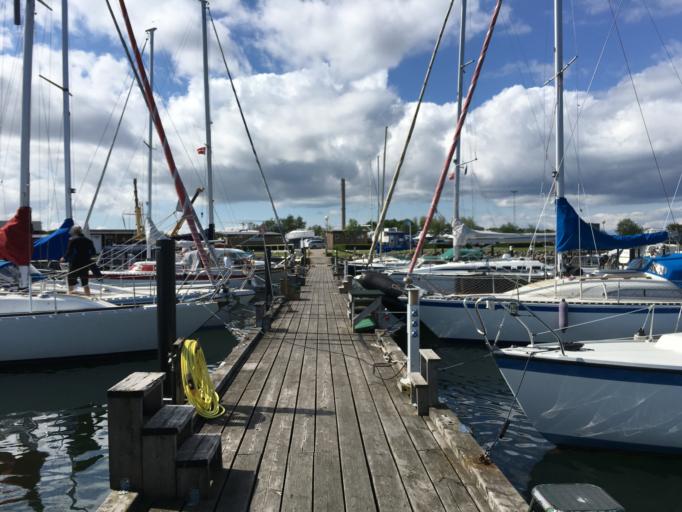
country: SE
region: Skane
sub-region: Malmo
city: Malmoe
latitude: 55.5970
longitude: 12.9365
